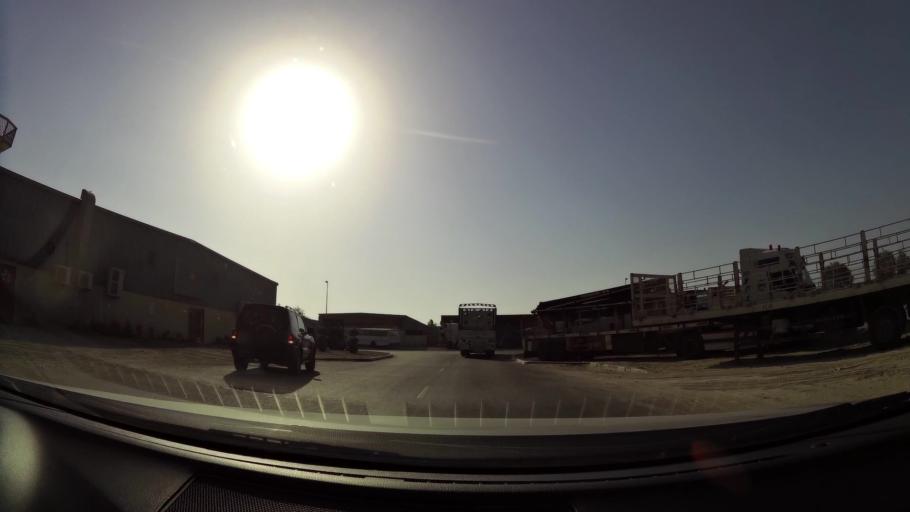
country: AE
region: Dubai
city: Dubai
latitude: 25.1227
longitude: 55.2389
